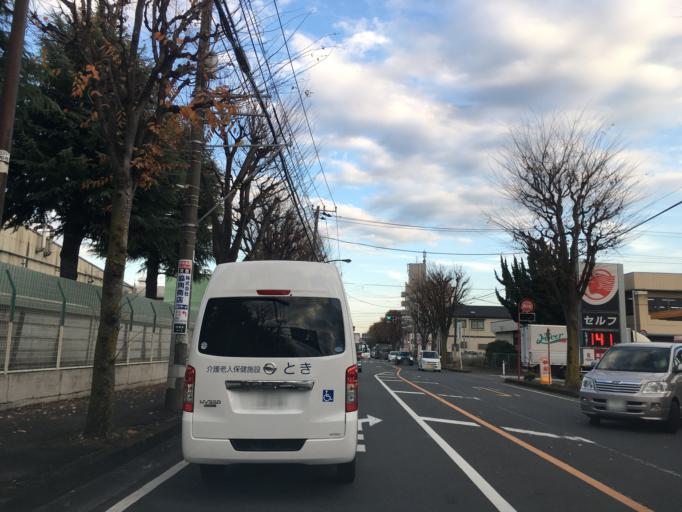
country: JP
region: Kanagawa
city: Zama
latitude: 35.5711
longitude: 139.3535
